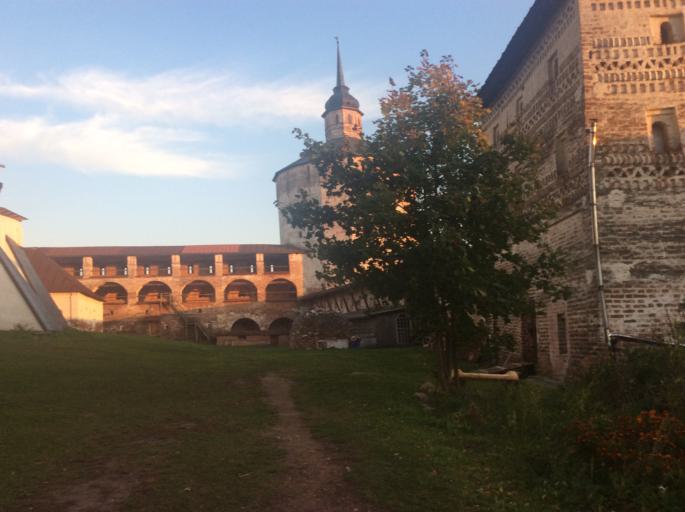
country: RU
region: Vologda
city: Kirillov
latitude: 59.8564
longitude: 38.3692
